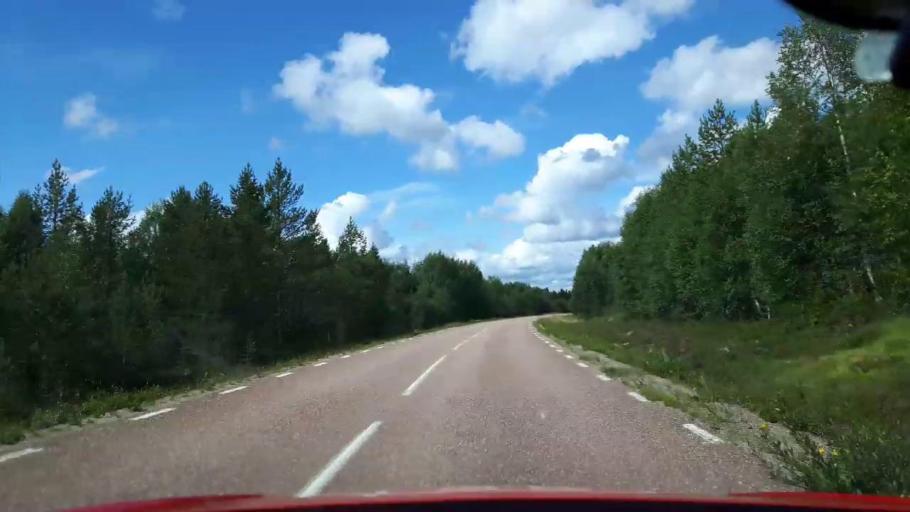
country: SE
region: Dalarna
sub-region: Alvdalens Kommun
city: AElvdalen
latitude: 61.7996
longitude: 13.6718
